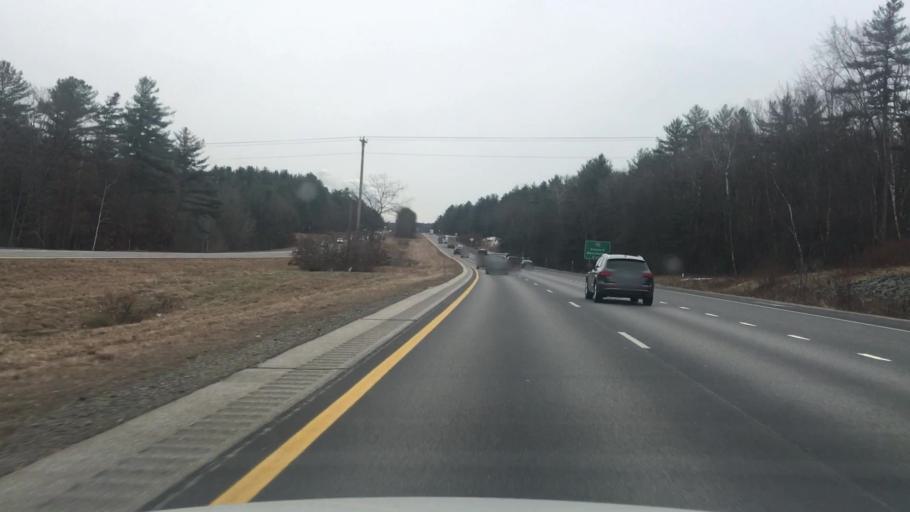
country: US
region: New Hampshire
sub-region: Merrimack County
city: Concord
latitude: 43.1774
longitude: -71.5623
